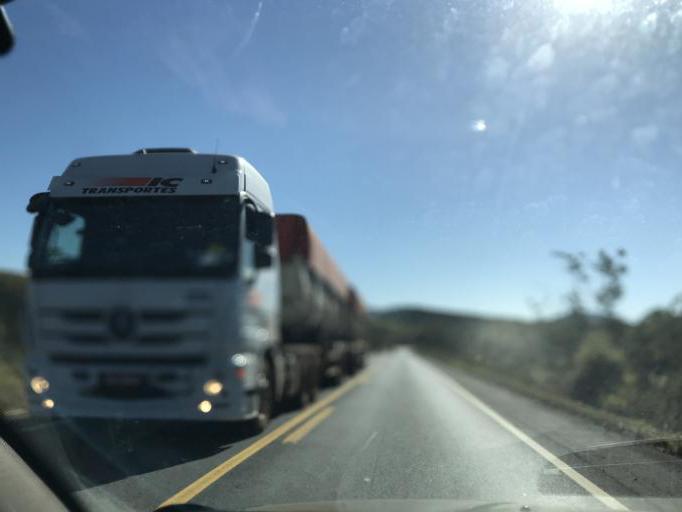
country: BR
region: Minas Gerais
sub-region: Bambui
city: Bambui
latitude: -19.8323
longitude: -46.0050
